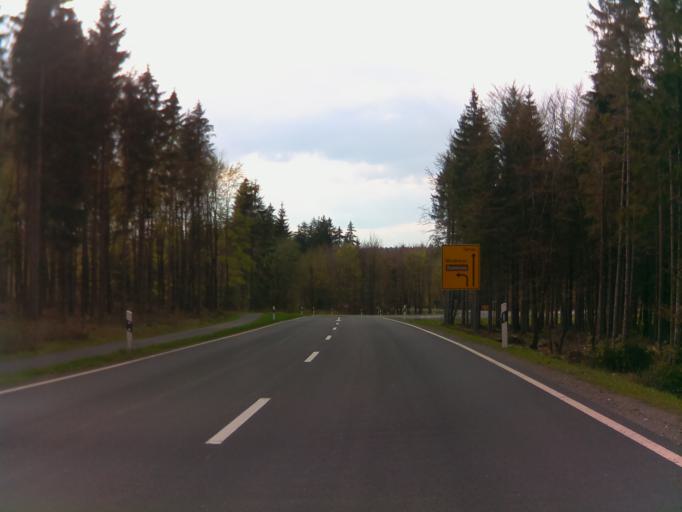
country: DE
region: Bavaria
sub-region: Upper Franconia
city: Ludwigsstadt
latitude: 50.4499
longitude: 11.3557
